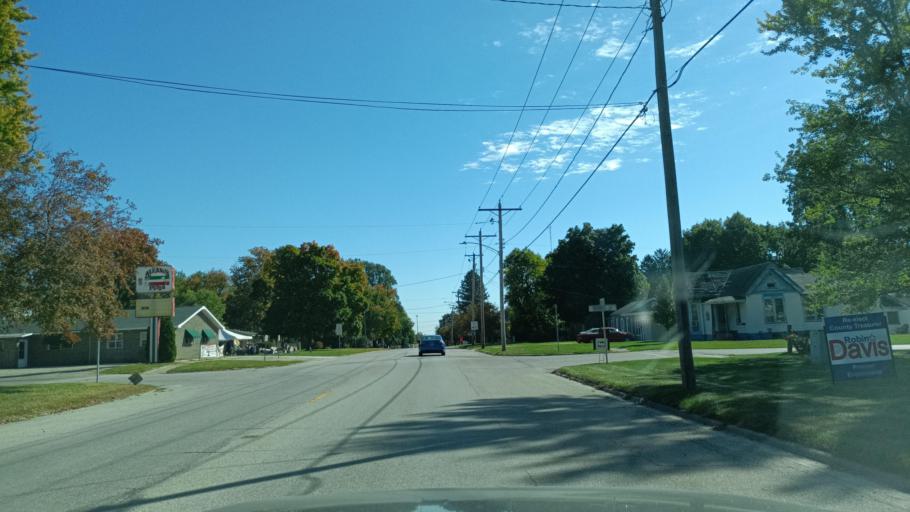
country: US
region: Illinois
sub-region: Knox County
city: Knoxville
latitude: 40.9079
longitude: -90.2743
